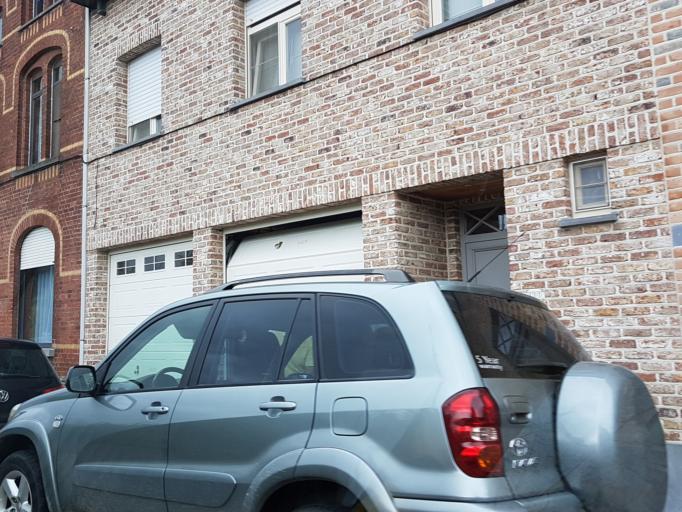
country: BE
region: Flanders
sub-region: Provincie Oost-Vlaanderen
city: Aalst
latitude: 50.9505
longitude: 4.0262
